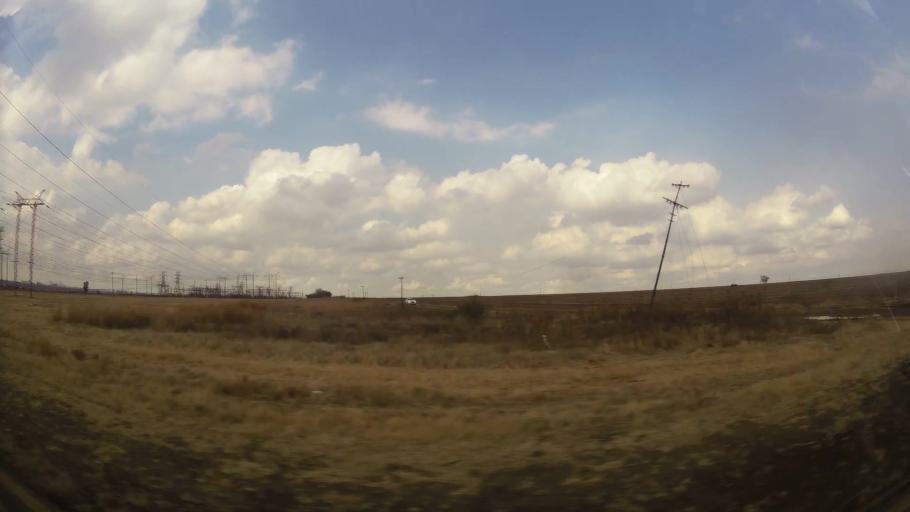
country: ZA
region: Orange Free State
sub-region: Fezile Dabi District Municipality
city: Sasolburg
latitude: -26.8236
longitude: 27.9030
